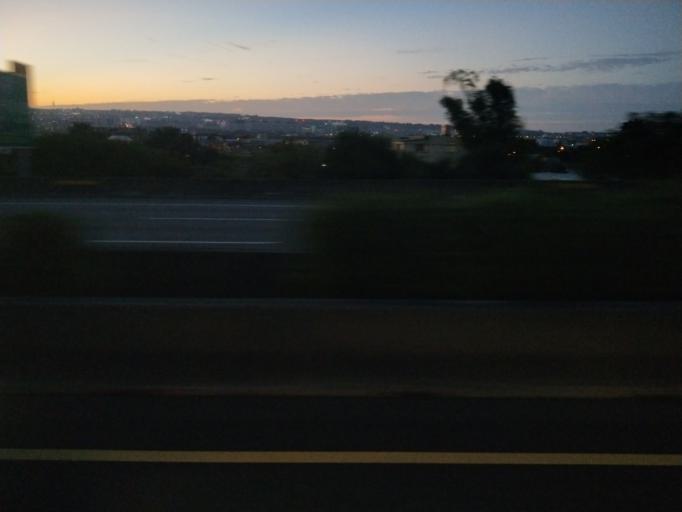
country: TW
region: Taiwan
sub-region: Taichung City
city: Taichung
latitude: 24.1948
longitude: 120.6417
